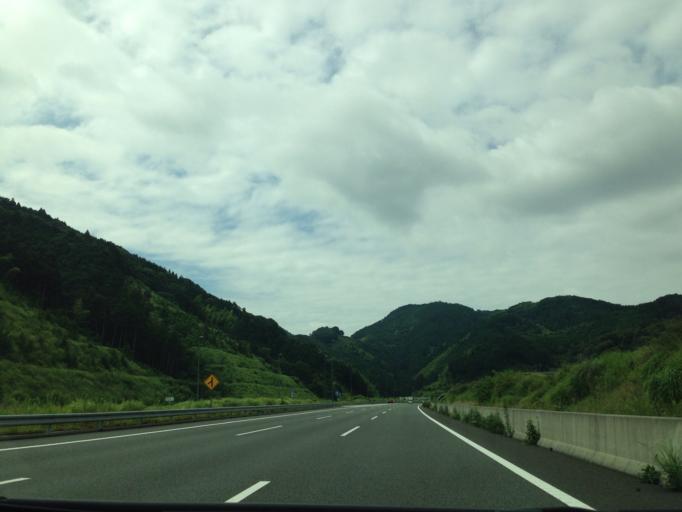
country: JP
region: Shizuoka
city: Shizuoka-shi
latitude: 34.9695
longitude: 138.2923
